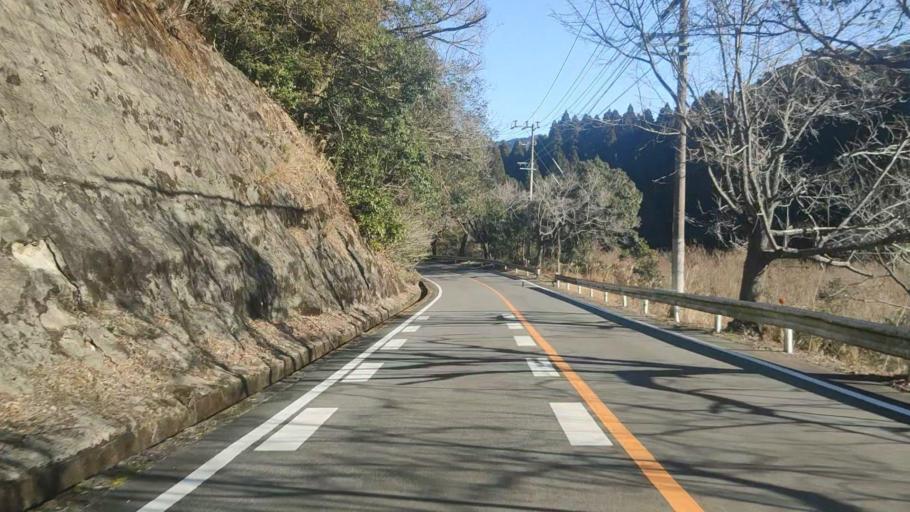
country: JP
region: Miyazaki
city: Nobeoka
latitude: 32.6377
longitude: 131.7423
